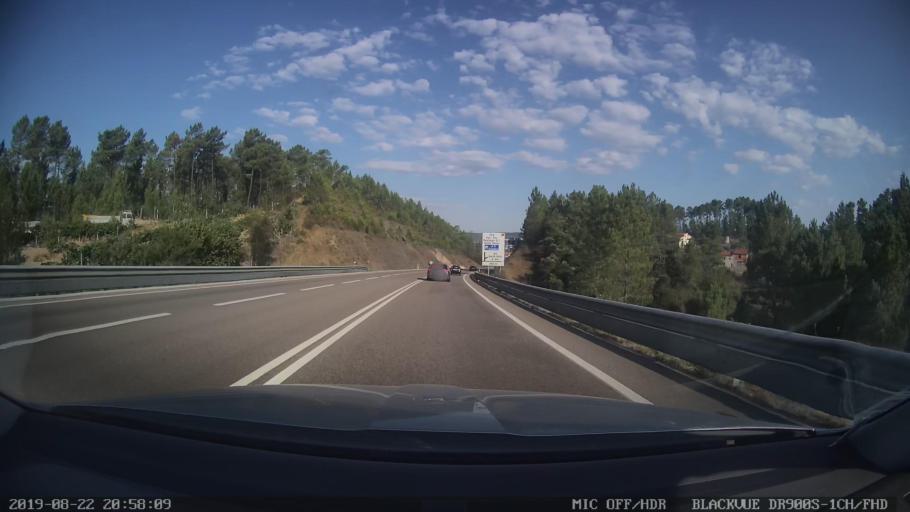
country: PT
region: Castelo Branco
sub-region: Serta
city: Serta
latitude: 39.7978
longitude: -8.0775
